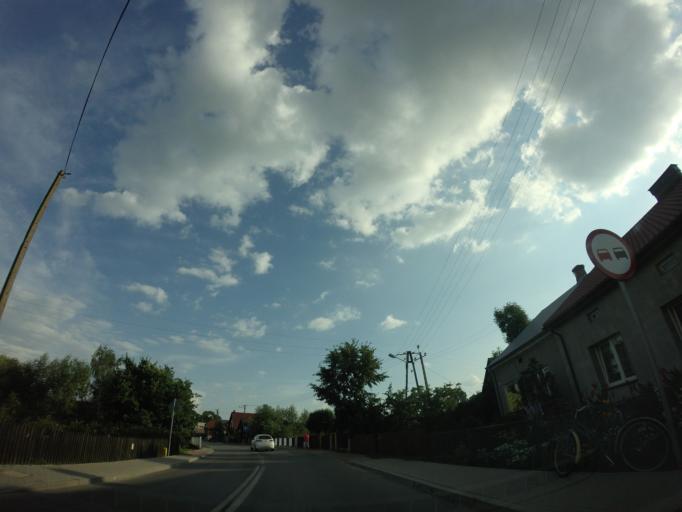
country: PL
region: Lublin Voivodeship
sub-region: Powiat lubartowski
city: Jeziorzany
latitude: 51.6028
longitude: 22.2766
